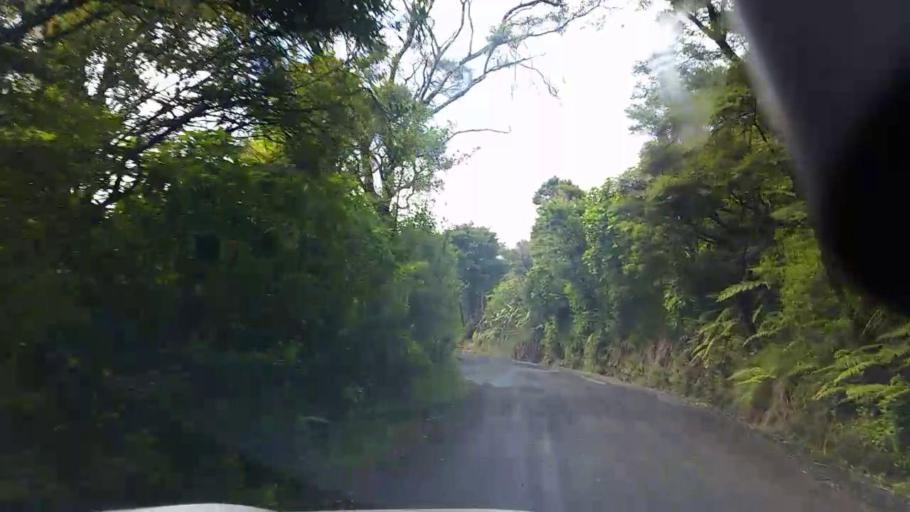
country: NZ
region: Auckland
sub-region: Auckland
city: Muriwai Beach
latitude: -36.9339
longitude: 174.5045
